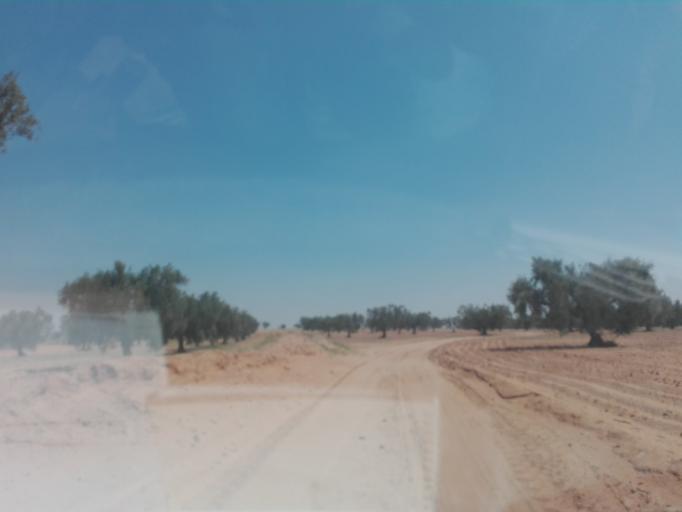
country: TN
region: Safaqis
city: Bi'r `Ali Bin Khalifah
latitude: 34.6121
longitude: 10.3471
